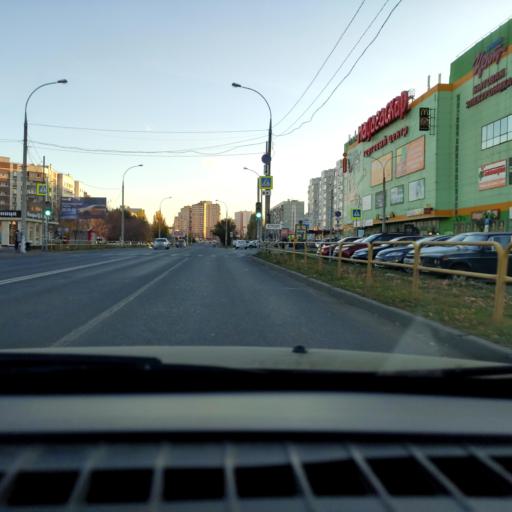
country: RU
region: Samara
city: Tol'yatti
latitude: 53.5448
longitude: 49.3612
